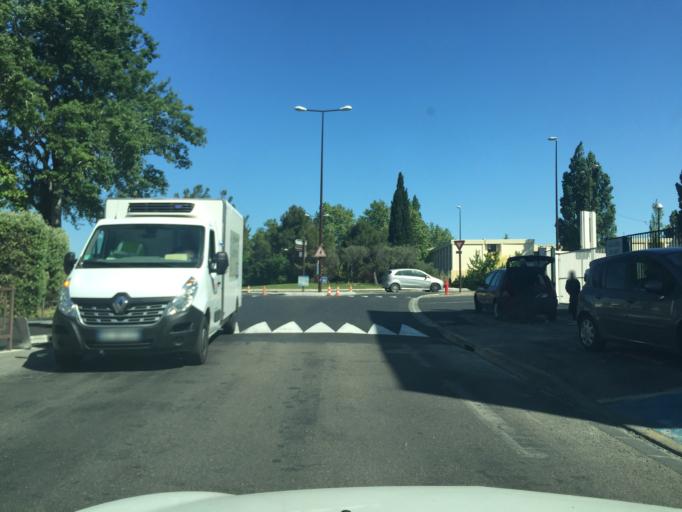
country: FR
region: Provence-Alpes-Cote d'Azur
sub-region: Departement du Vaucluse
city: Le Pontet
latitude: 43.9456
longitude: 4.8418
